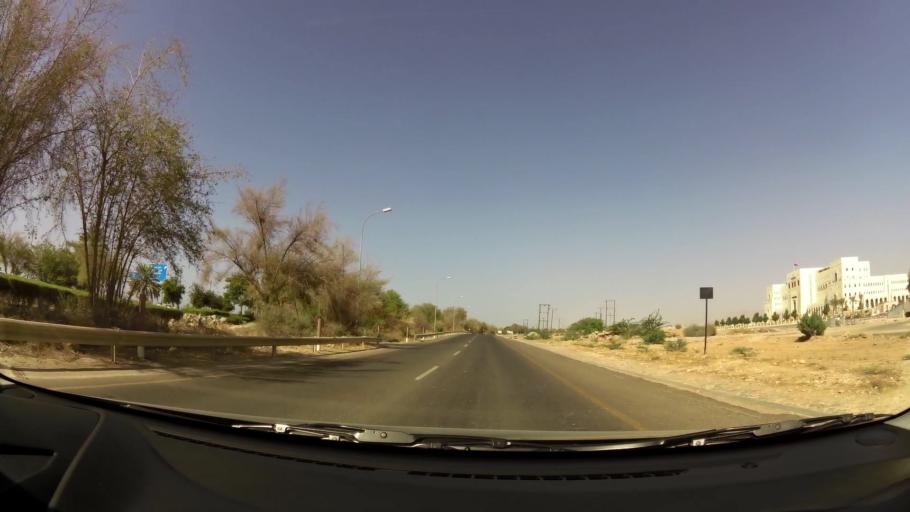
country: OM
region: Muhafazat Masqat
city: Bawshar
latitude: 23.5897
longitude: 58.3224
